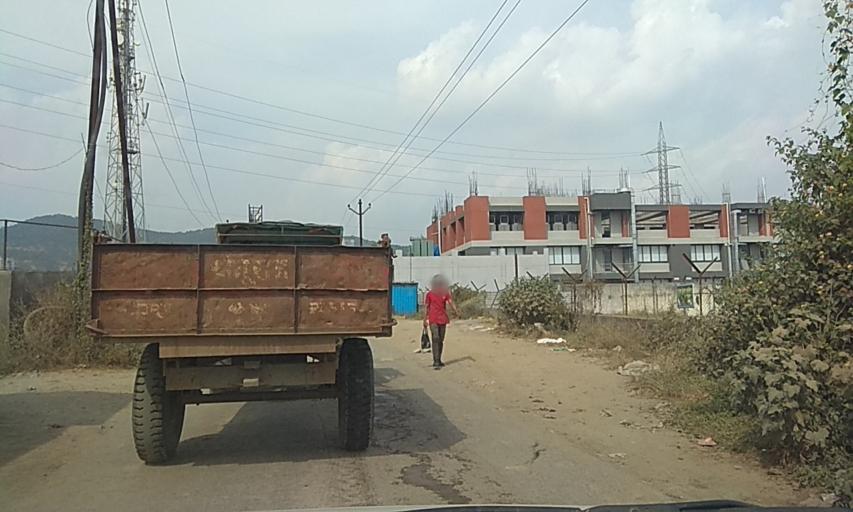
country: IN
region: Maharashtra
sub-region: Pune Division
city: Pimpri
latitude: 18.5881
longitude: 73.7055
